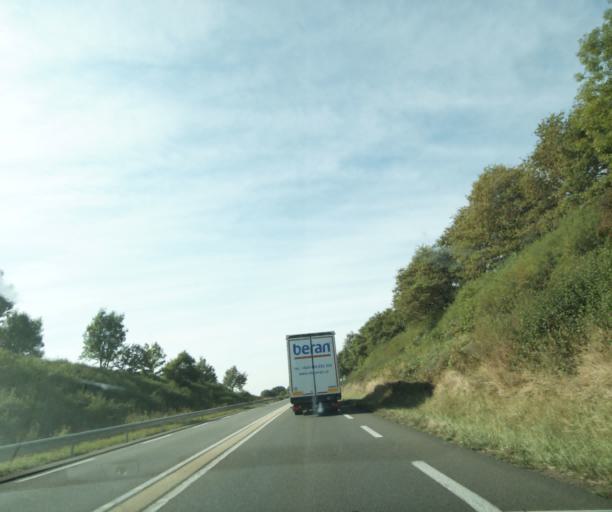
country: FR
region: Bourgogne
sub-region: Departement de Saone-et-Loire
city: Genelard
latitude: 46.5831
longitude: 4.2184
